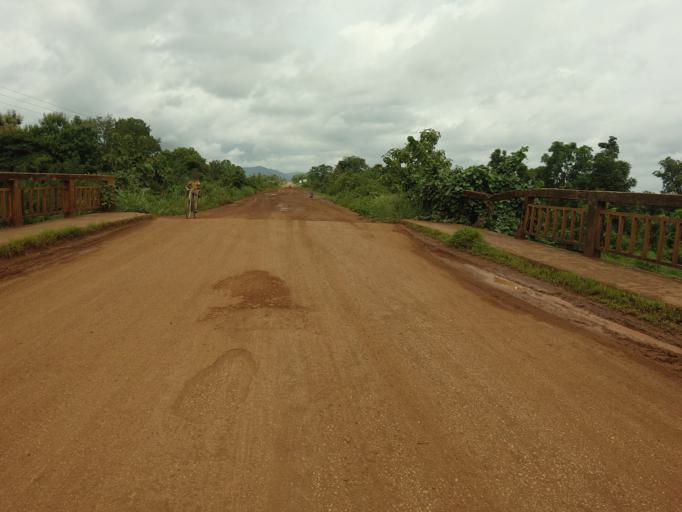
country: GH
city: Kpandae
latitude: 8.2793
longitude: 0.5069
